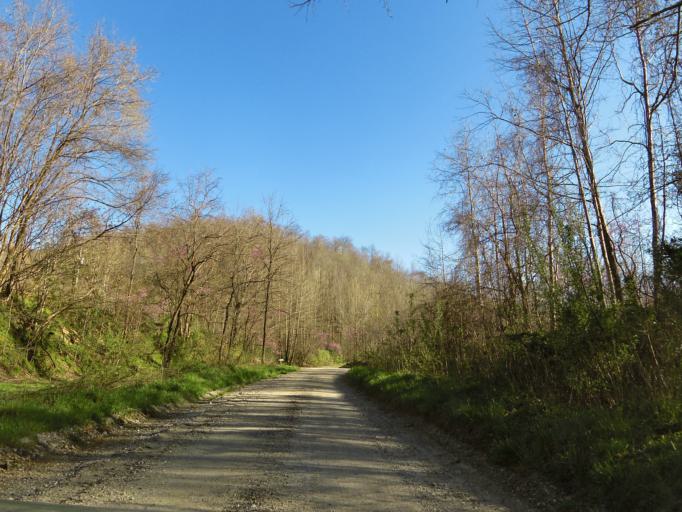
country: US
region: Tennessee
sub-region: Roane County
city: Oliver Springs
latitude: 36.2155
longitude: -84.4149
